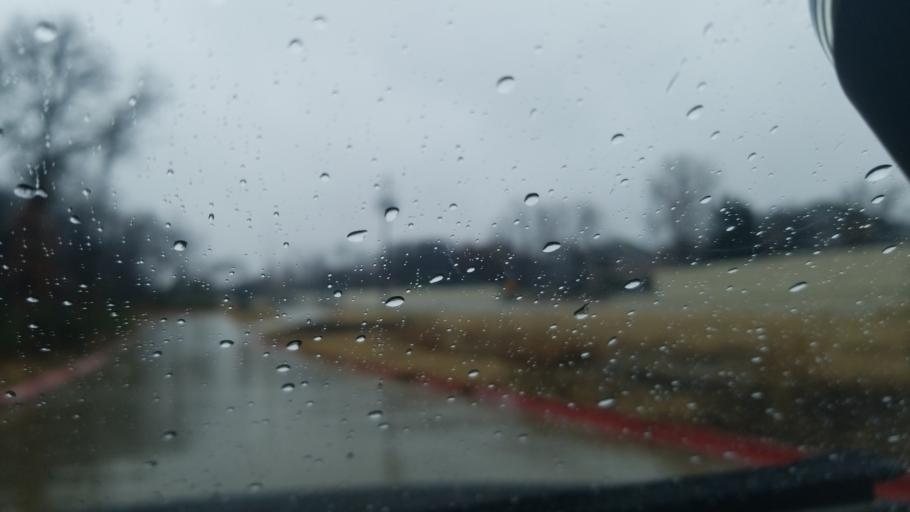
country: US
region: Texas
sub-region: Denton County
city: Corinth
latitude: 33.1337
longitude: -97.0947
